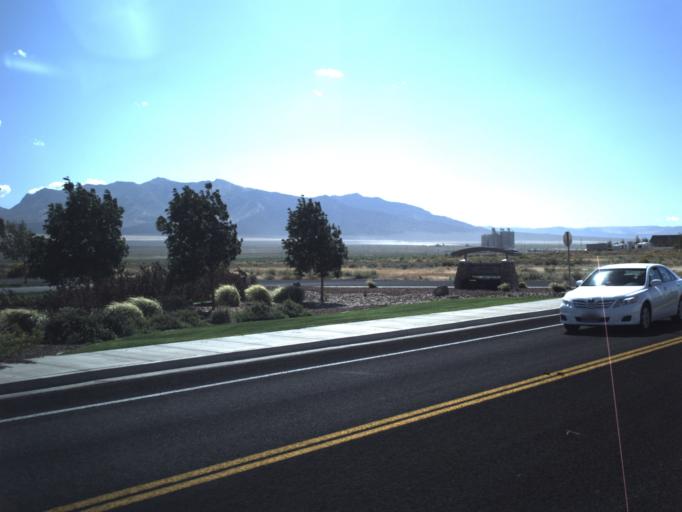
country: US
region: Utah
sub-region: Beaver County
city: Milford
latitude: 38.4069
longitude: -113.0099
